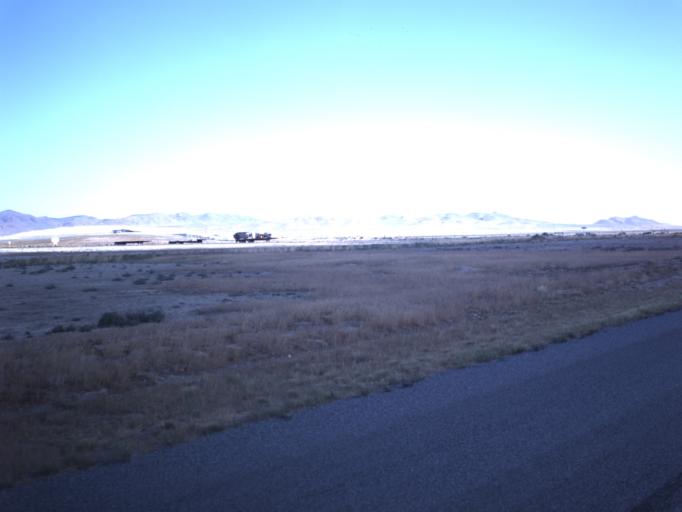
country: US
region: Utah
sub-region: Millard County
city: Delta
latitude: 38.9356
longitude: -112.8089
